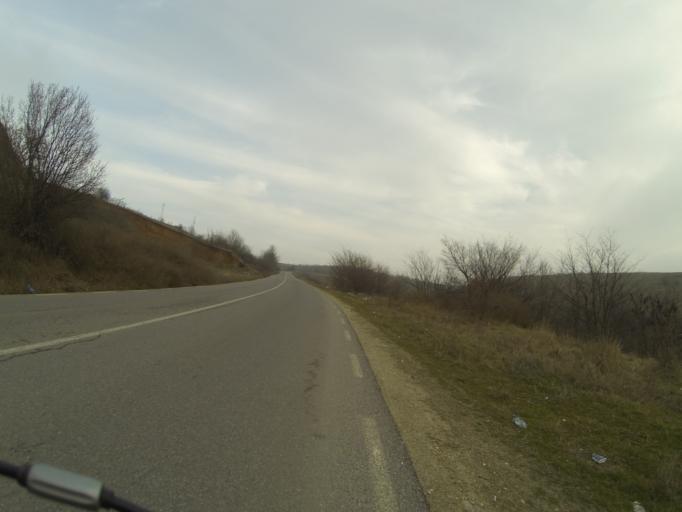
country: RO
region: Mehedinti
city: Vanju-Mare
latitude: 44.4122
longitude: 22.8801
